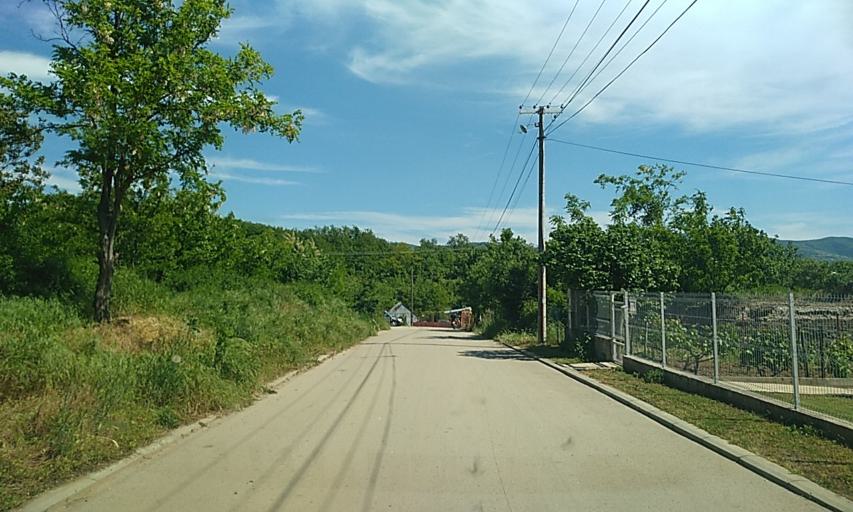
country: RS
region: Central Serbia
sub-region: Nisavski Okrug
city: Nis
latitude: 43.2900
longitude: 21.8659
